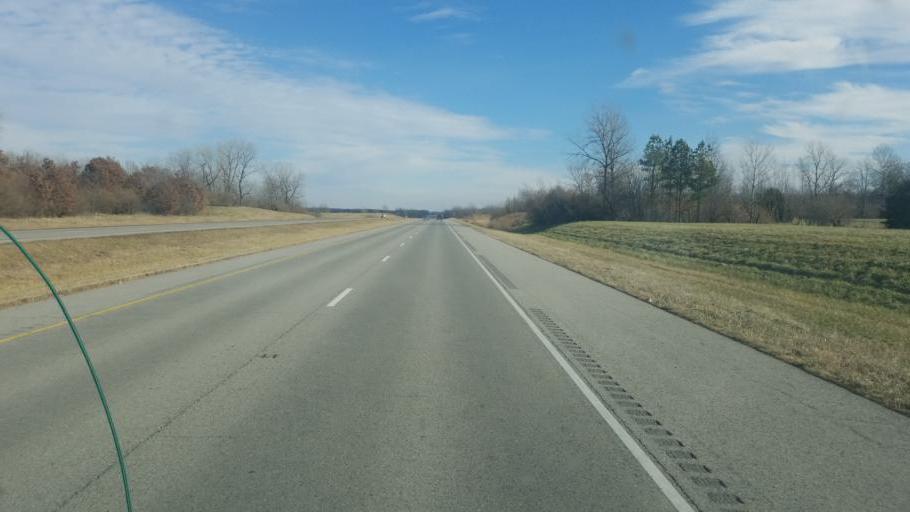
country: US
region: Illinois
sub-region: Saline County
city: Carrier Mills
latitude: 37.7302
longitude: -88.7793
